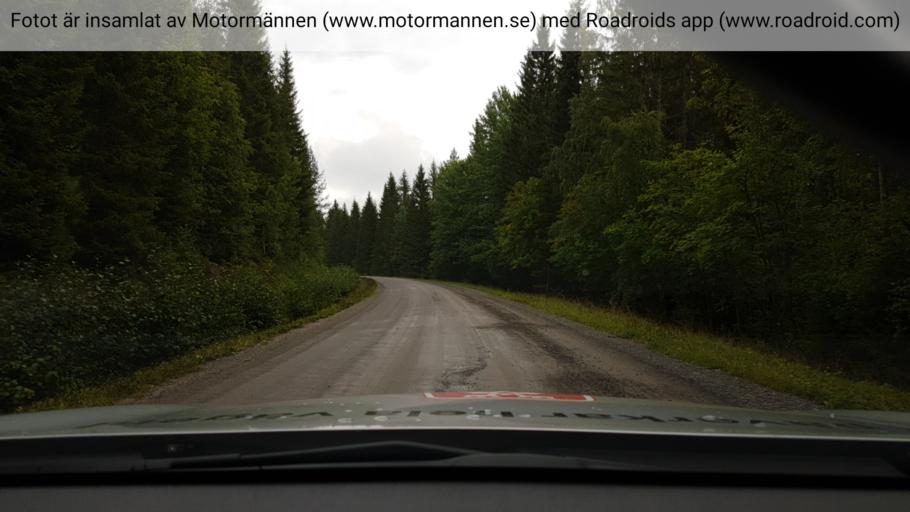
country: SE
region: Vaesterbotten
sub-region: Skelleftea Kommun
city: Burtraesk
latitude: 64.3483
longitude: 20.5388
